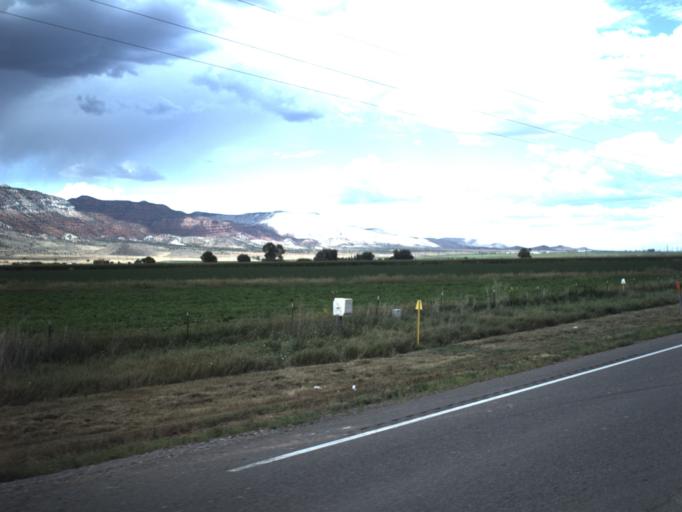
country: US
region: Utah
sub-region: Sevier County
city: Richfield
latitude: 38.8015
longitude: -112.0289
